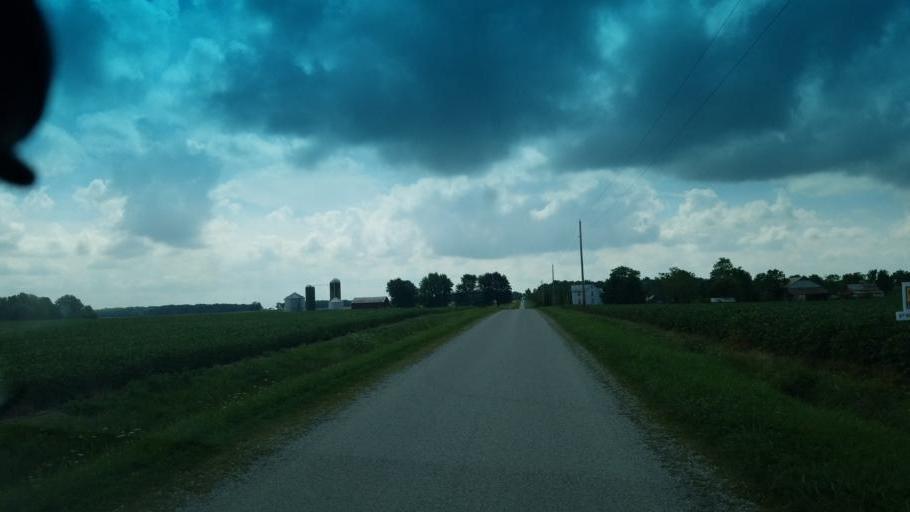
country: US
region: Ohio
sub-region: Crawford County
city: Bucyrus
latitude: 40.9777
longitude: -82.9013
